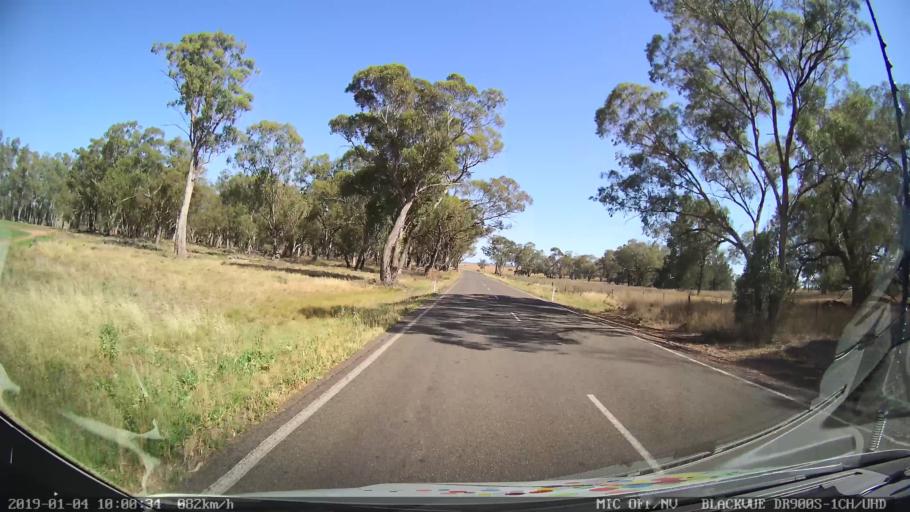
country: AU
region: New South Wales
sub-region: Cabonne
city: Canowindra
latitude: -33.4961
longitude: 148.3781
